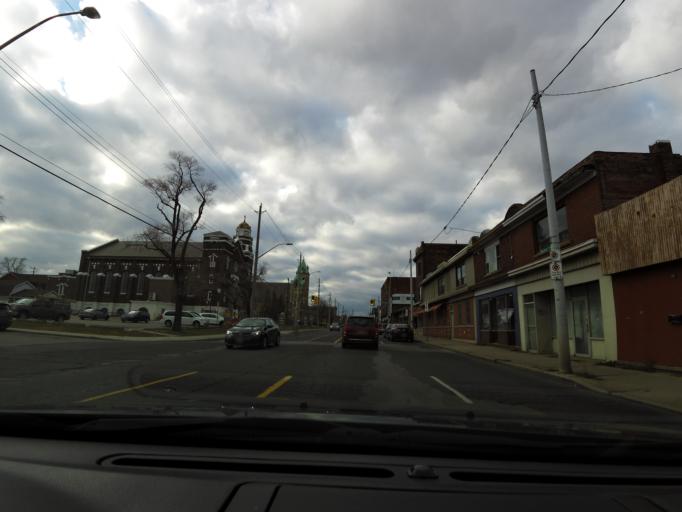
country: CA
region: Ontario
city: Hamilton
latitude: 43.2559
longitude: -79.8338
